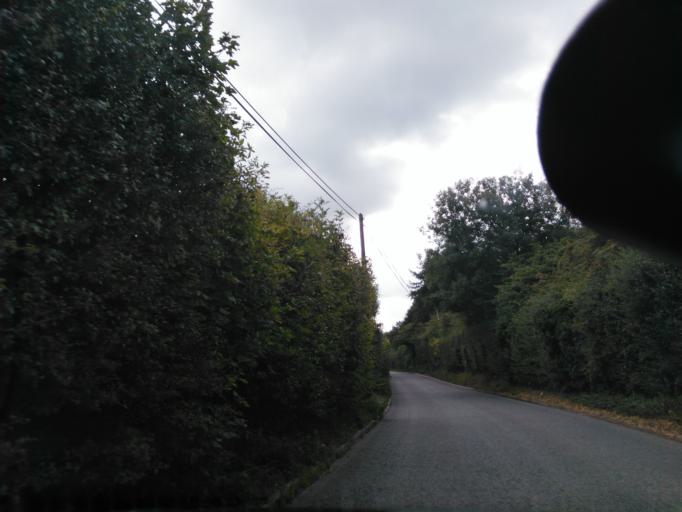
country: GB
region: England
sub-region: Dorset
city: Shaftesbury
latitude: 50.9987
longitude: -2.1789
